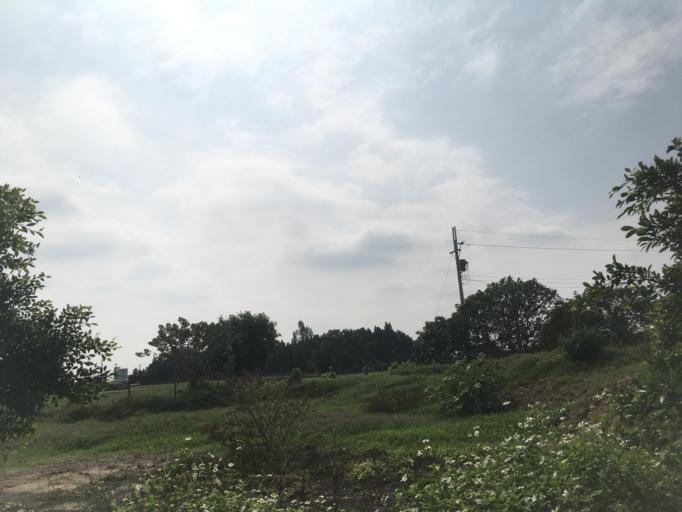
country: TW
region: Taiwan
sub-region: Yunlin
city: Douliu
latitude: 23.6942
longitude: 120.4568
